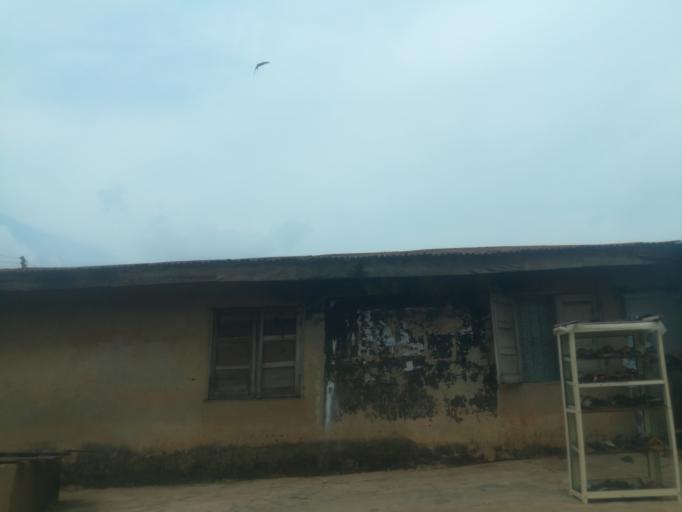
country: NG
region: Oyo
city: Ibadan
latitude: 7.4297
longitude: 3.9177
